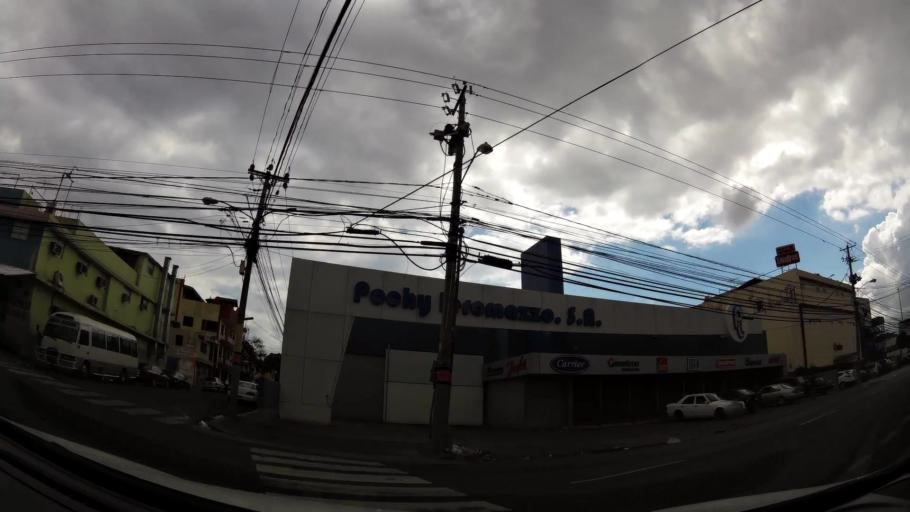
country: DO
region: Nacional
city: San Carlos
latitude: 18.4847
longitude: -69.9156
